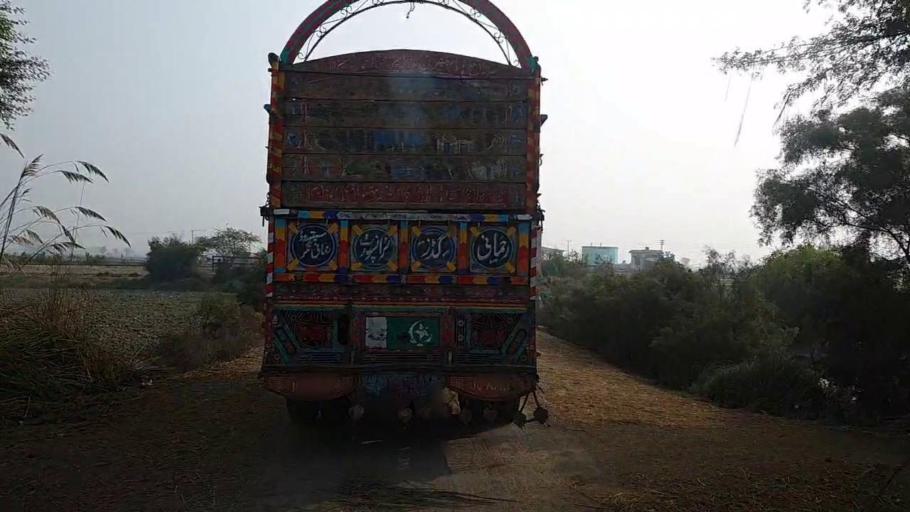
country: PK
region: Sindh
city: Dadu
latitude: 26.8400
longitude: 67.7792
